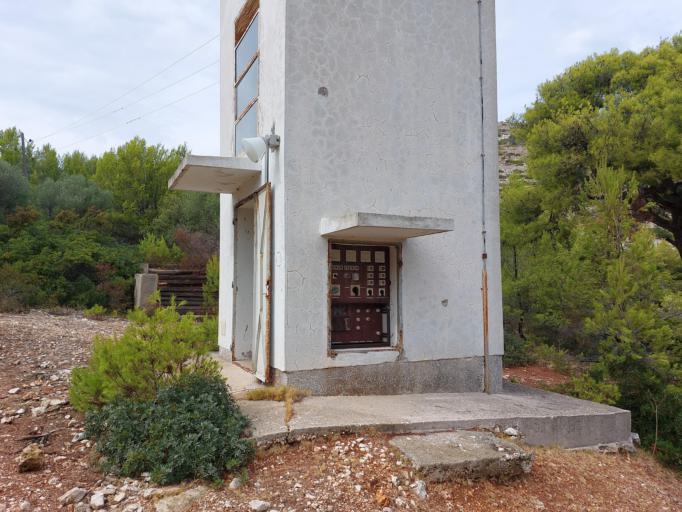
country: HR
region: Dubrovacko-Neretvanska
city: Smokvica
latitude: 42.7326
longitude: 16.8393
